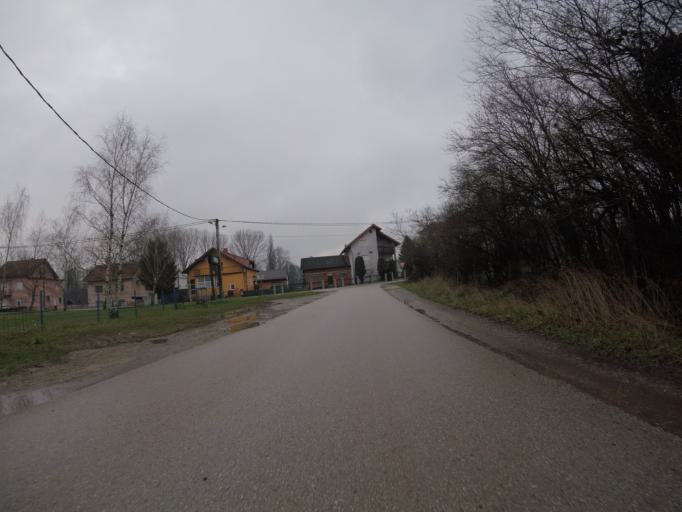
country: HR
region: Zagrebacka
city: Kuce
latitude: 45.7040
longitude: 16.1276
